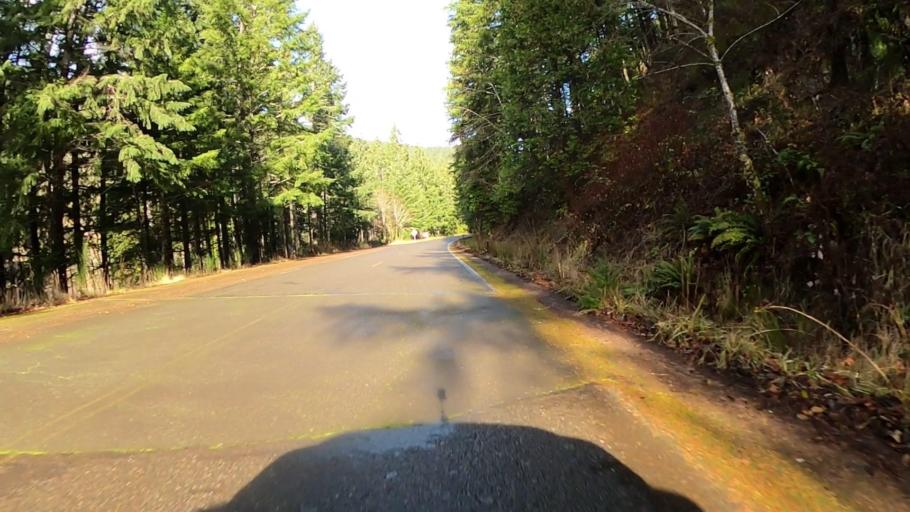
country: US
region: Oregon
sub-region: Lane County
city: Oakridge
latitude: 43.7662
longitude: -122.4887
